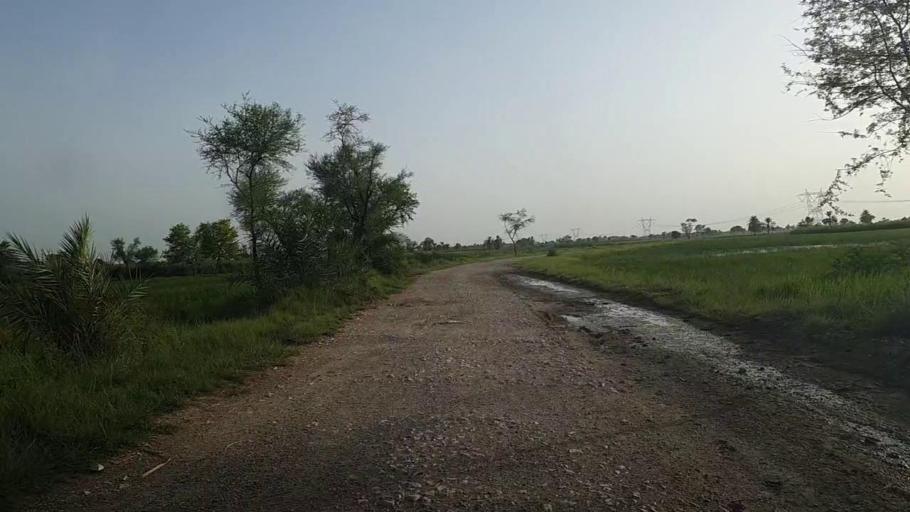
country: PK
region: Sindh
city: Naushahro Firoz
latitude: 26.8062
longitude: 68.1222
